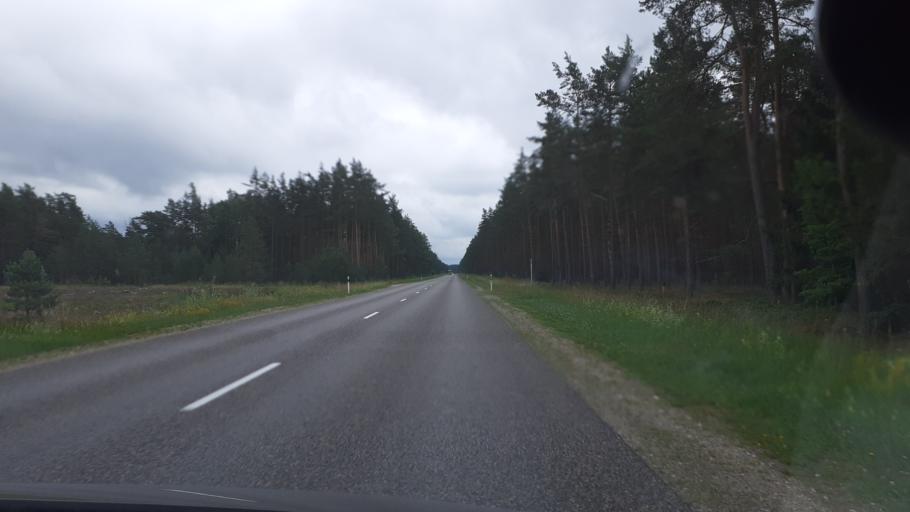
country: LV
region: Ventspils Rajons
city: Piltene
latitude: 57.1323
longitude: 21.7286
